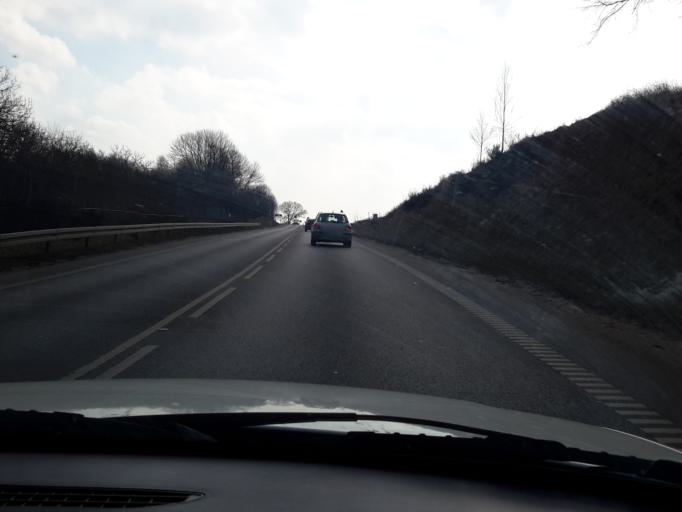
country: PL
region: Pomeranian Voivodeship
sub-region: Powiat wejherowski
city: Rekowo Dolne
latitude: 54.6582
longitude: 18.3620
